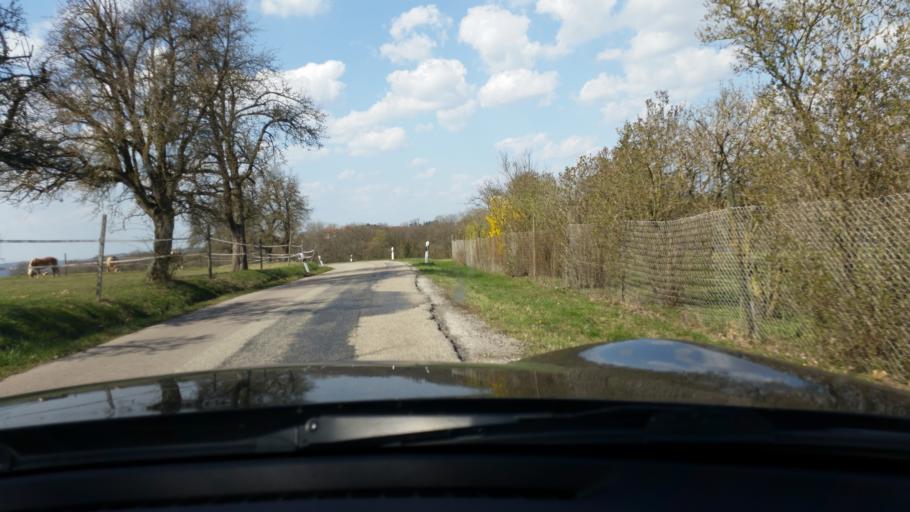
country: DE
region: Baden-Wuerttemberg
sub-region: Regierungsbezirk Stuttgart
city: Braunsbach
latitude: 49.2630
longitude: 9.7849
